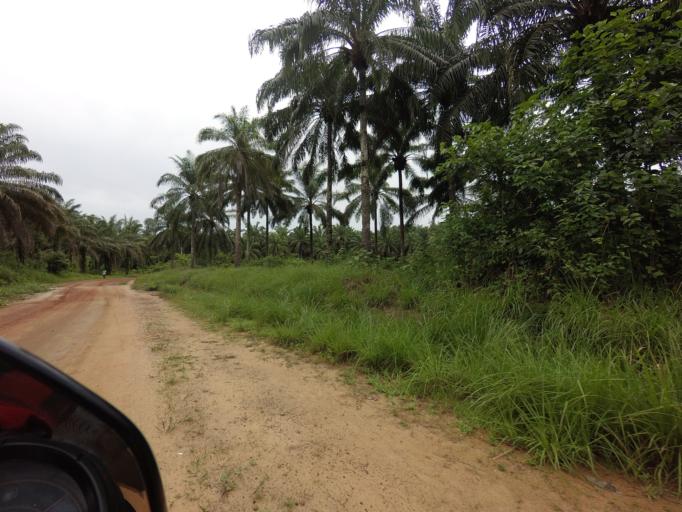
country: SL
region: Eastern Province
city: Mobai
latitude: 7.9935
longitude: -10.7378
